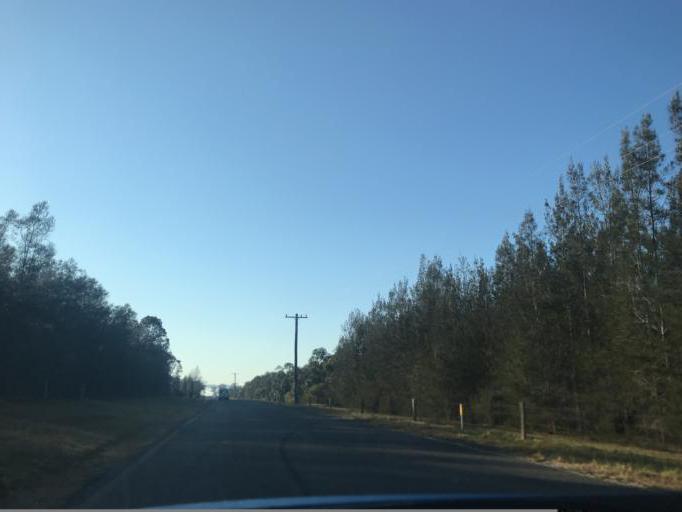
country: AU
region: New South Wales
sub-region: Cessnock
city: Cessnock
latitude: -32.9080
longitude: 151.2908
